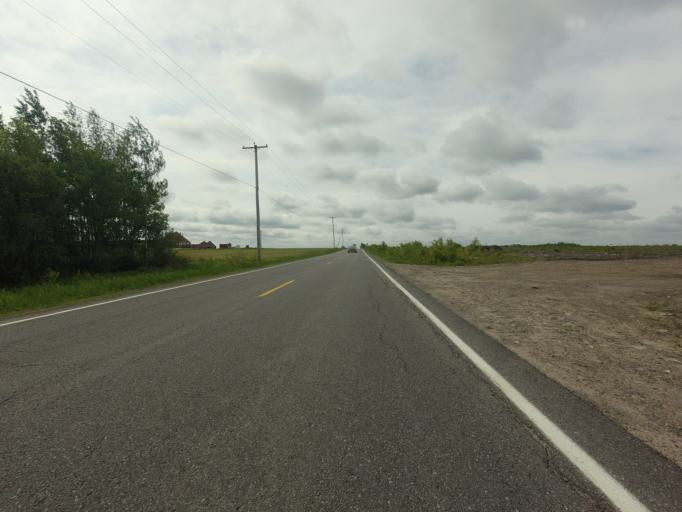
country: CA
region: Ontario
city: Cornwall
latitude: 44.7730
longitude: -74.6723
